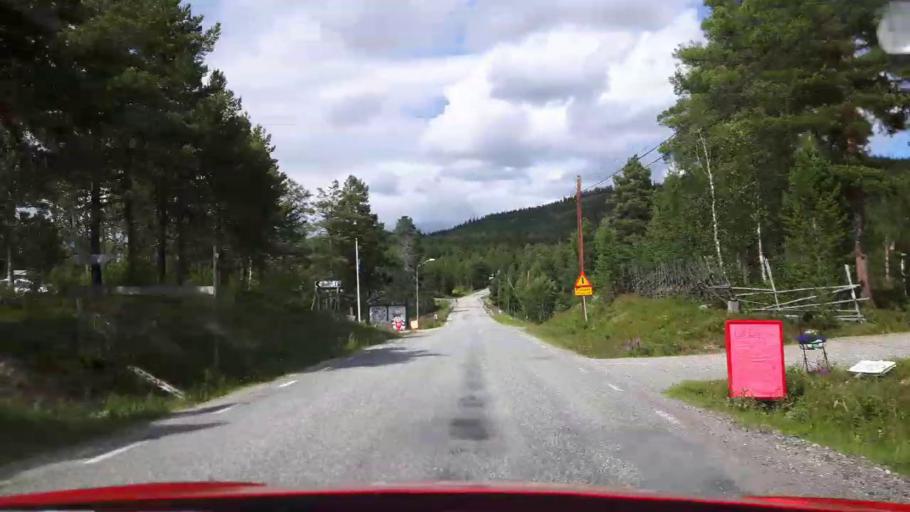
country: NO
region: Hedmark
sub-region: Engerdal
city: Engerdal
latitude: 62.4341
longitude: 12.6789
